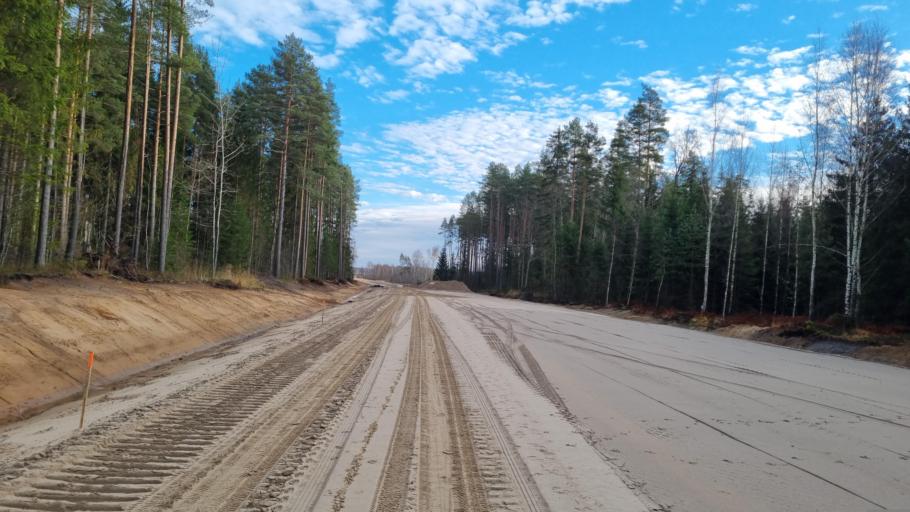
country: LV
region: Kekava
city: Kekava
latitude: 56.7889
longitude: 24.2191
